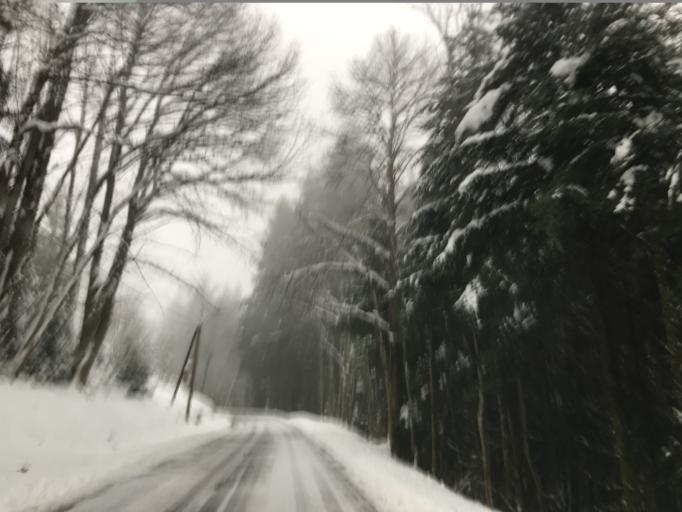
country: FR
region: Rhone-Alpes
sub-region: Departement de la Loire
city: Noiretable
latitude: 45.7394
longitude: 3.6817
